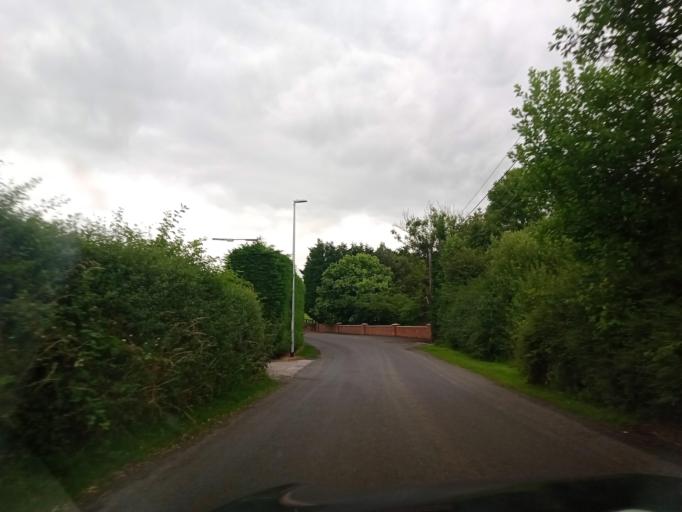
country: IE
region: Leinster
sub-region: Kilkenny
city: Castlecomer
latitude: 52.8930
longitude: -7.1529
